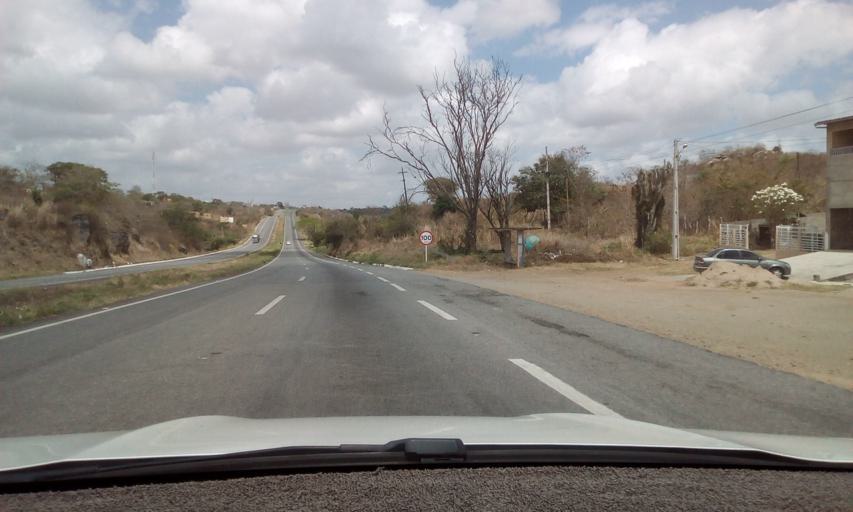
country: BR
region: Paraiba
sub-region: Massaranduba
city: Massaranduba
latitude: -7.2567
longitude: -35.8157
